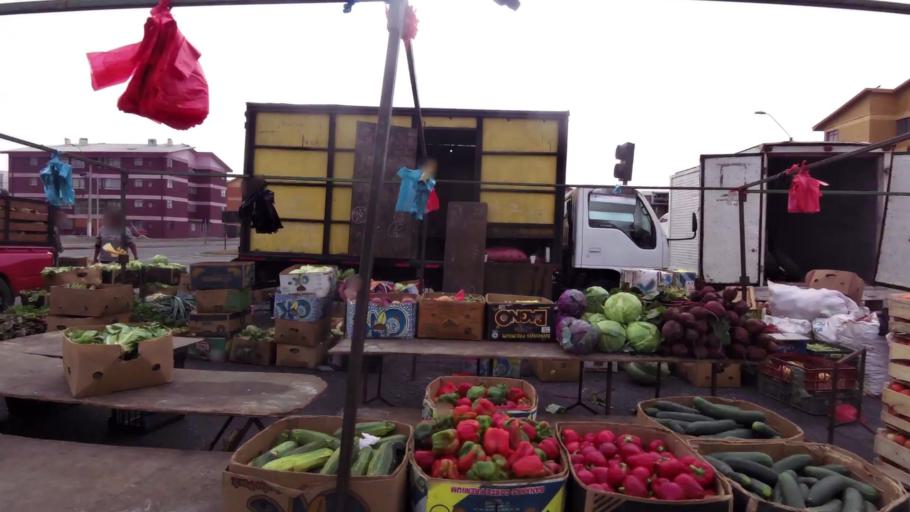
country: CL
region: Biobio
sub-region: Provincia de Concepcion
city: Concepcion
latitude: -36.7911
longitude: -73.0944
